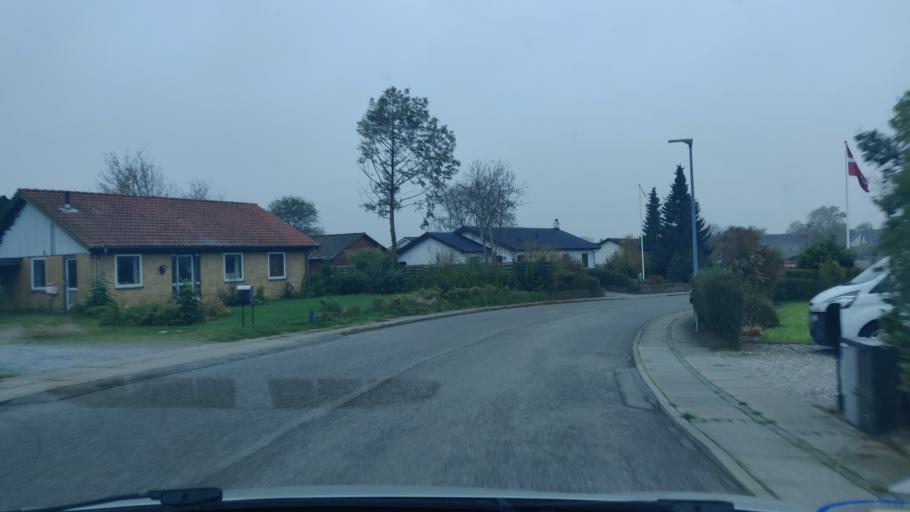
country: DK
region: South Denmark
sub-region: Kolding Kommune
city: Kolding
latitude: 55.5663
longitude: 9.4081
